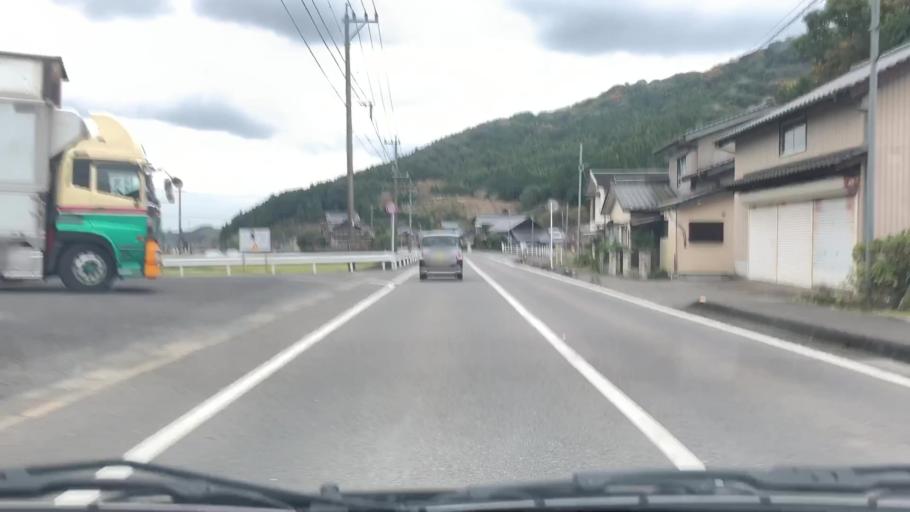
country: JP
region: Saga Prefecture
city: Kashima
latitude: 33.0995
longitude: 130.0576
